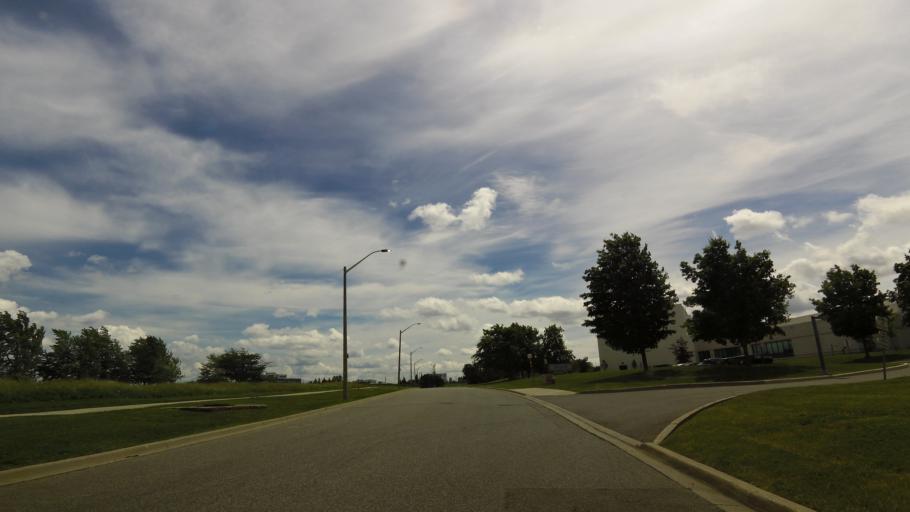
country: CA
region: Ontario
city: Mississauga
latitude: 43.5168
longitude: -79.6625
